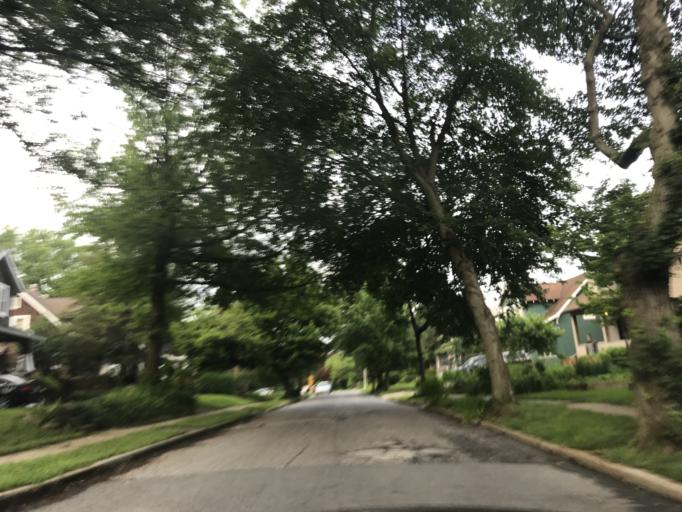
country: US
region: Maryland
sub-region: Baltimore County
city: Towson
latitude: 39.3691
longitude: -76.6070
